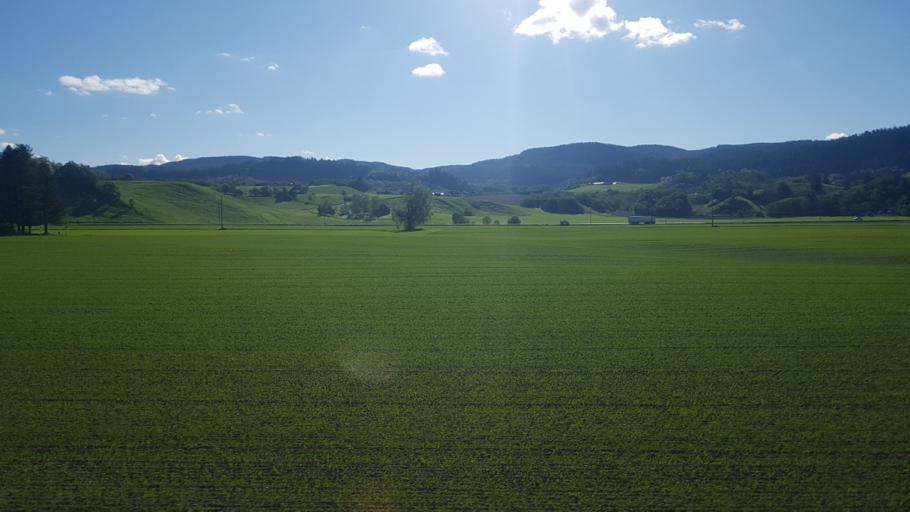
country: NO
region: Sor-Trondelag
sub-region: Melhus
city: Lundamo
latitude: 63.1810
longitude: 10.3104
